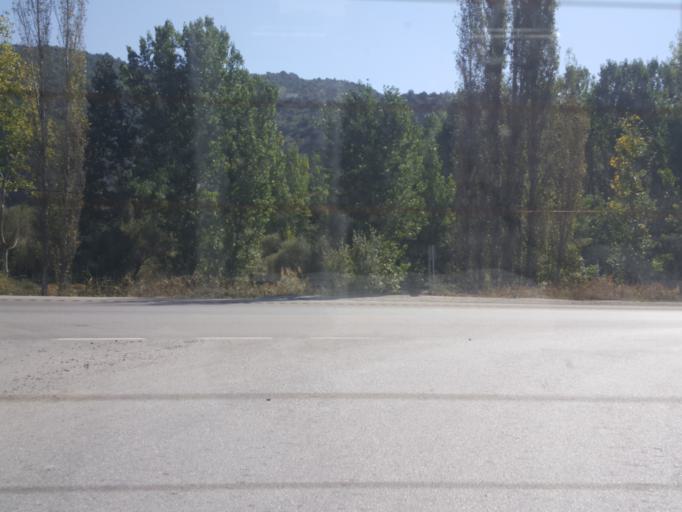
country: TR
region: Corum
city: Osmancik
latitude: 40.9762
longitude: 34.9152
